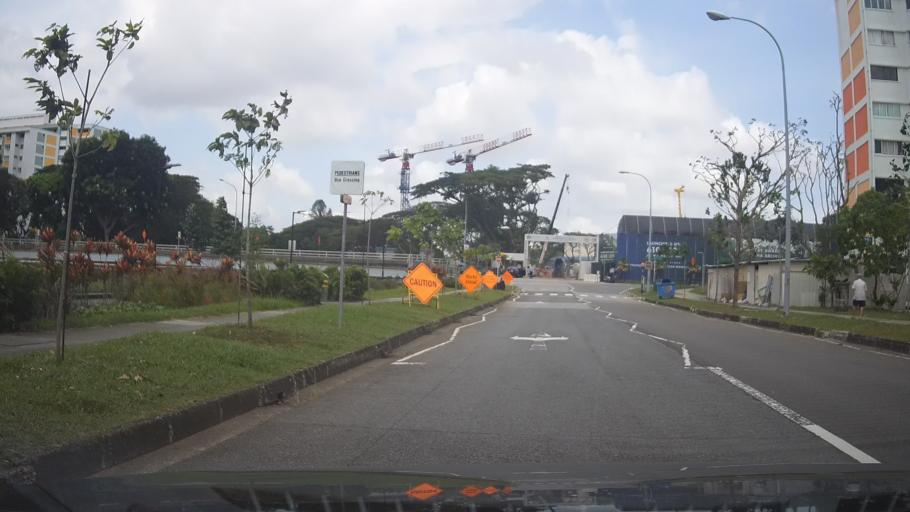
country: SG
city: Singapore
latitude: 1.3352
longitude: 103.8650
